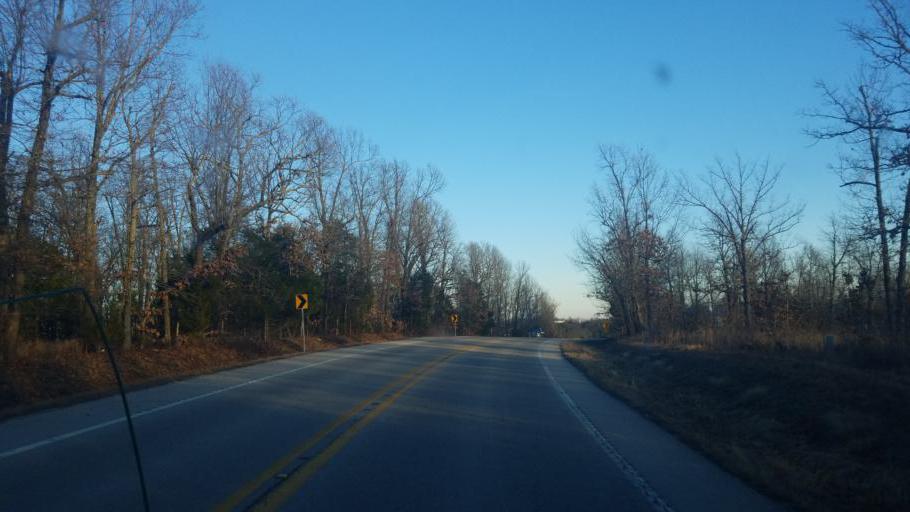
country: US
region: Arkansas
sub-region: Baxter County
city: Mountain Home
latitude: 36.3862
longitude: -92.1866
